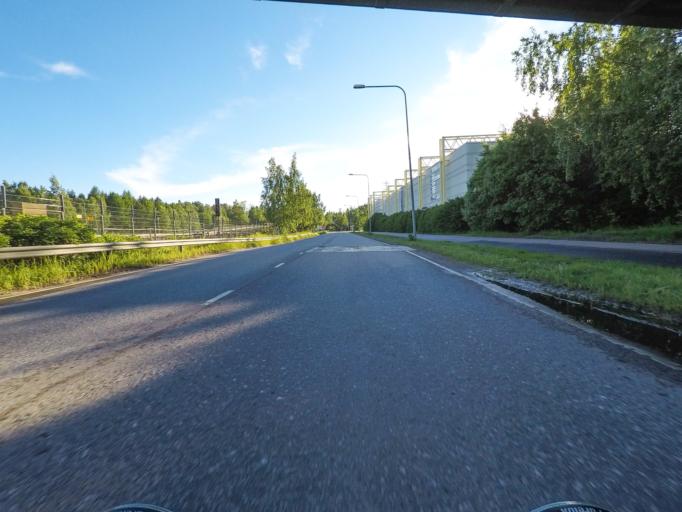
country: FI
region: Uusimaa
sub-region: Helsinki
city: Vantaa
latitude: 60.2090
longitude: 25.0702
